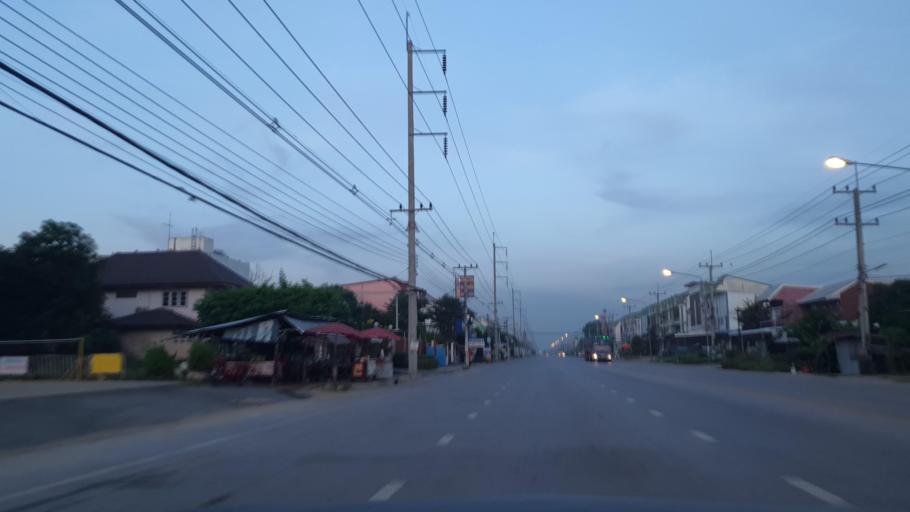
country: TH
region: Nakhon Sawan
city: Kao Liao
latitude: 15.7666
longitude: 99.9858
